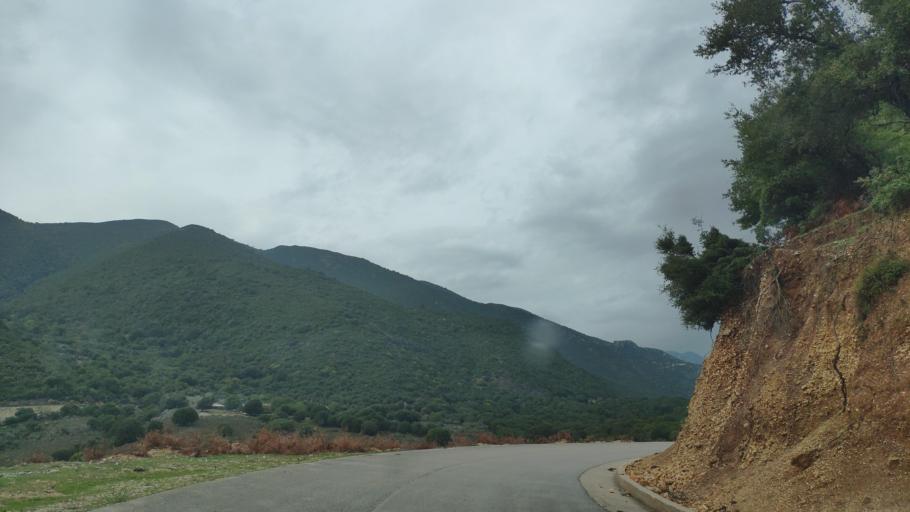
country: GR
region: Epirus
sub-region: Nomos Thesprotias
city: Paramythia
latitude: 39.3872
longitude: 20.6236
